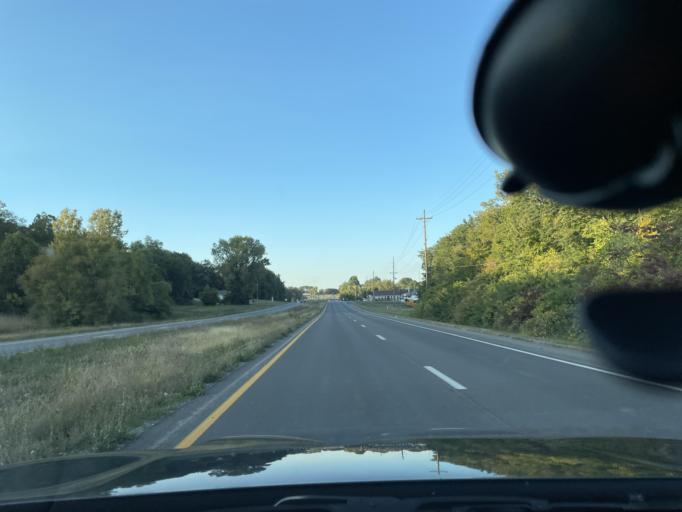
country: US
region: Missouri
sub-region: Andrew County
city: Country Club Village
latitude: 39.8074
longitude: -94.8409
